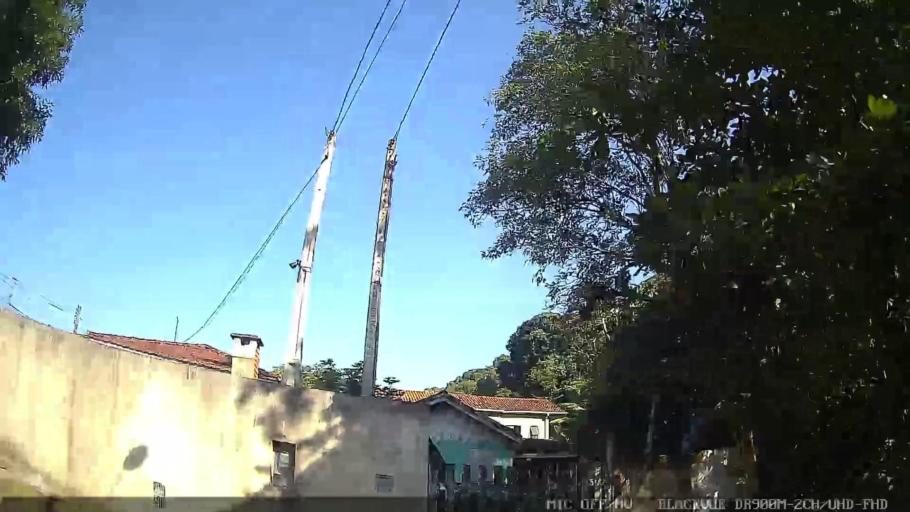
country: BR
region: Sao Paulo
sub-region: Guaruja
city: Guaruja
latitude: -24.0122
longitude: -46.2841
